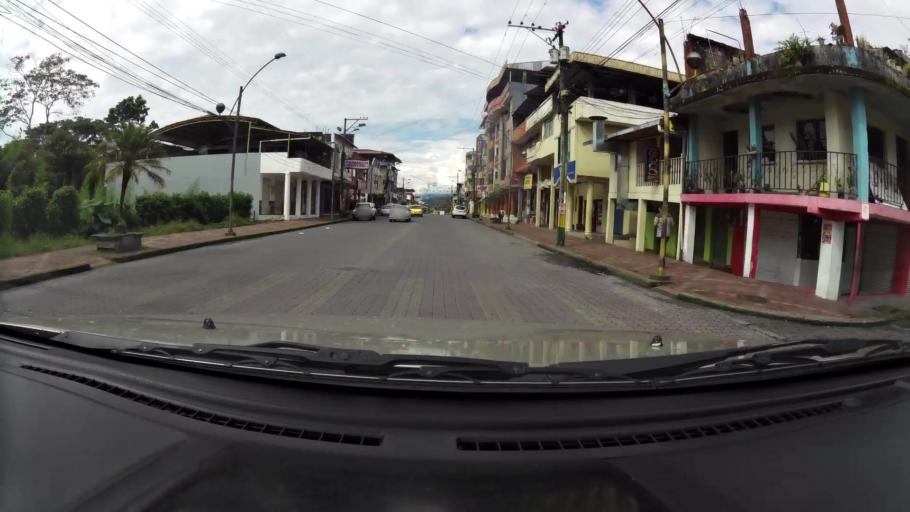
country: EC
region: Pastaza
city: Puyo
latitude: -1.4861
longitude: -78.0051
